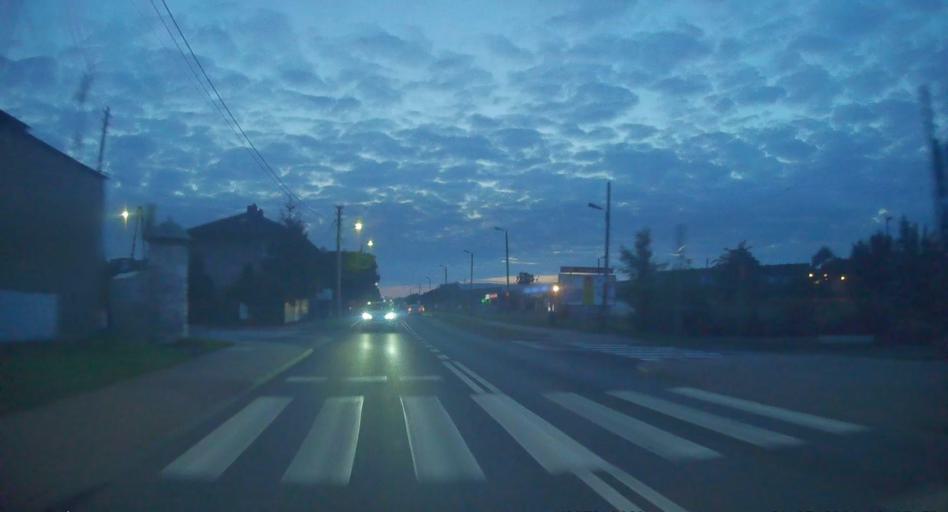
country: PL
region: Silesian Voivodeship
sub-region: Powiat klobucki
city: Klobuck
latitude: 50.9022
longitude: 18.9325
